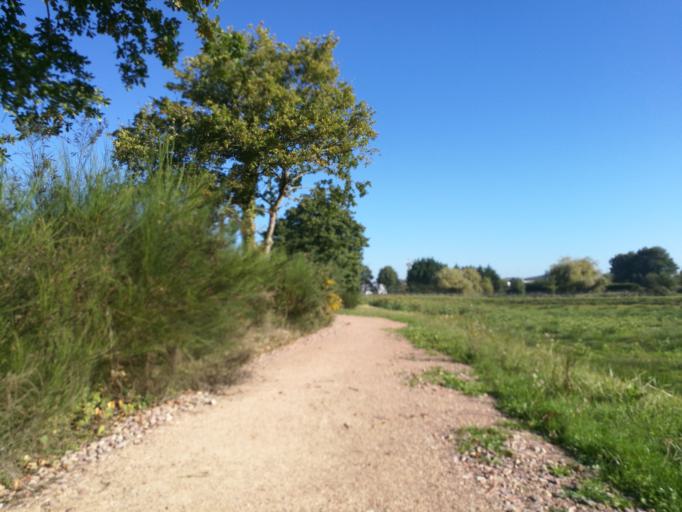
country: FR
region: Brittany
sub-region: Departement d'Ille-et-Vilaine
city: Bedee
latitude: 48.1757
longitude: -1.9319
